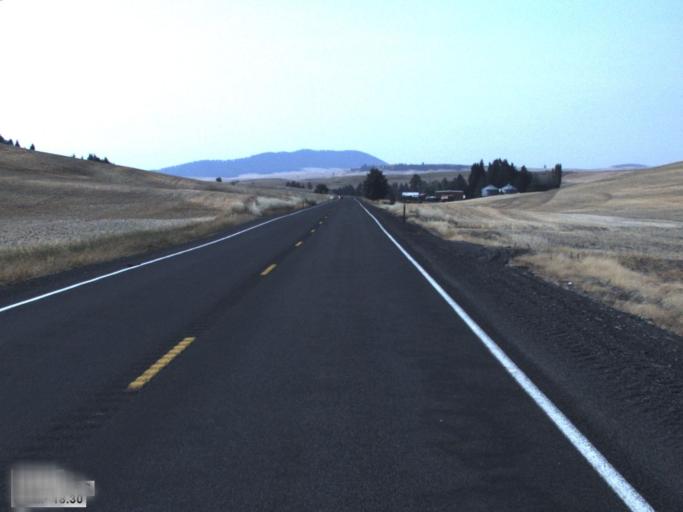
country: US
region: Washington
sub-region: Whitman County
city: Pullman
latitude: 46.9467
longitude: -117.0947
